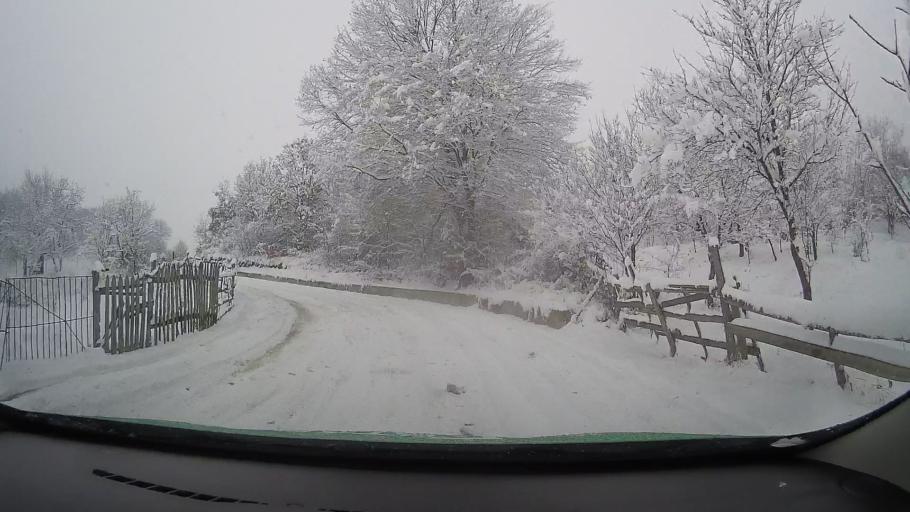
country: RO
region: Hunedoara
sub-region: Comuna Teliucu Inferior
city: Teliucu Inferior
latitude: 45.6984
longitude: 22.8911
